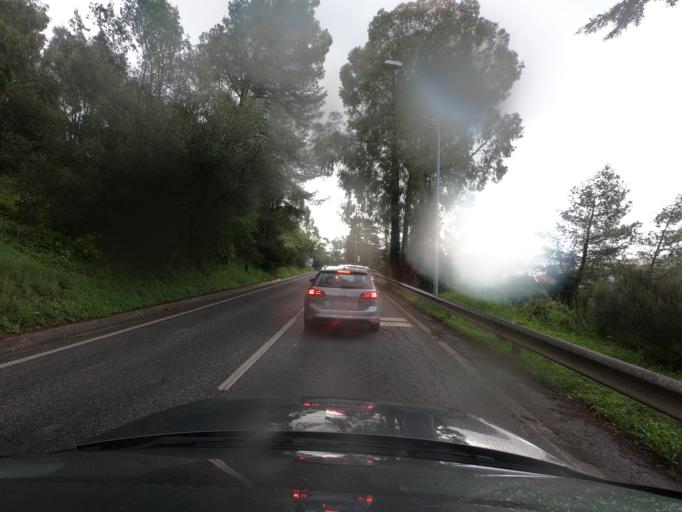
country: PT
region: Lisbon
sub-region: Oeiras
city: Carnaxide
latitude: 38.7256
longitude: -9.2548
